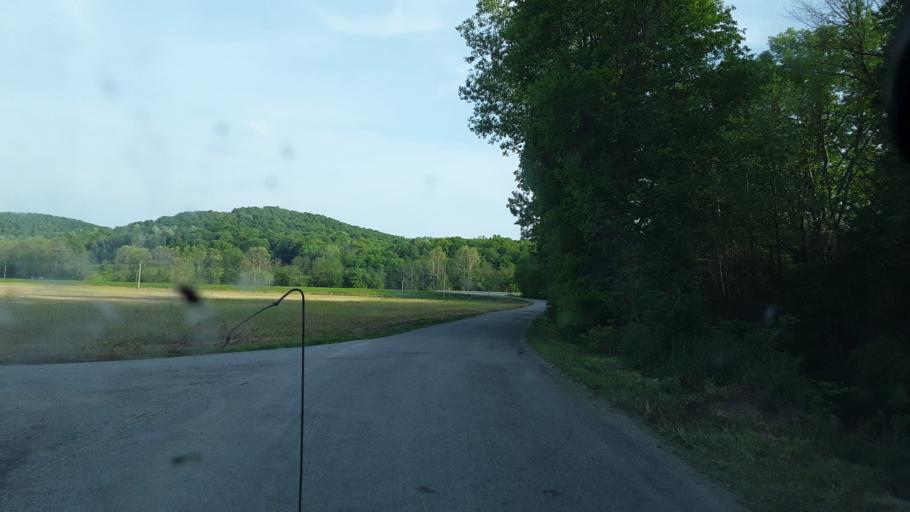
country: US
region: Ohio
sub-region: Ross County
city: Kingston
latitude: 39.4960
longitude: -82.7251
